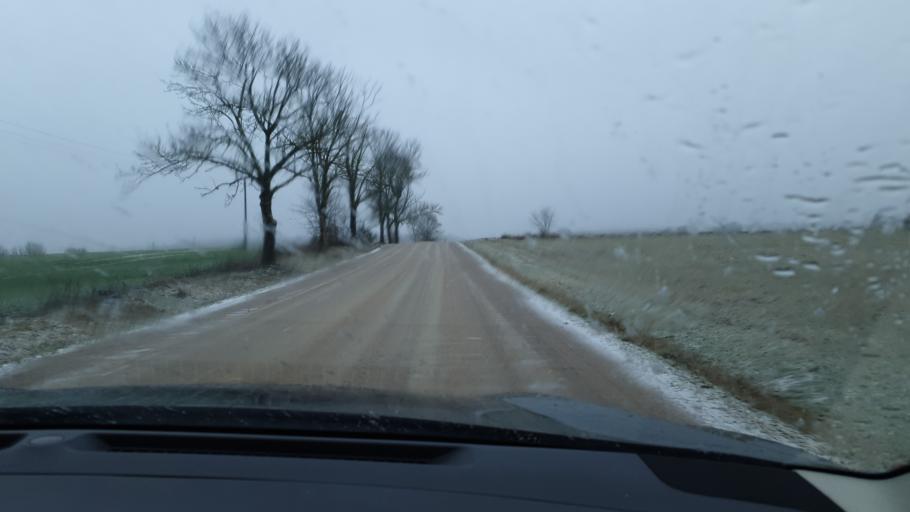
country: LT
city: Jieznas
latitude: 54.5805
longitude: 24.3167
